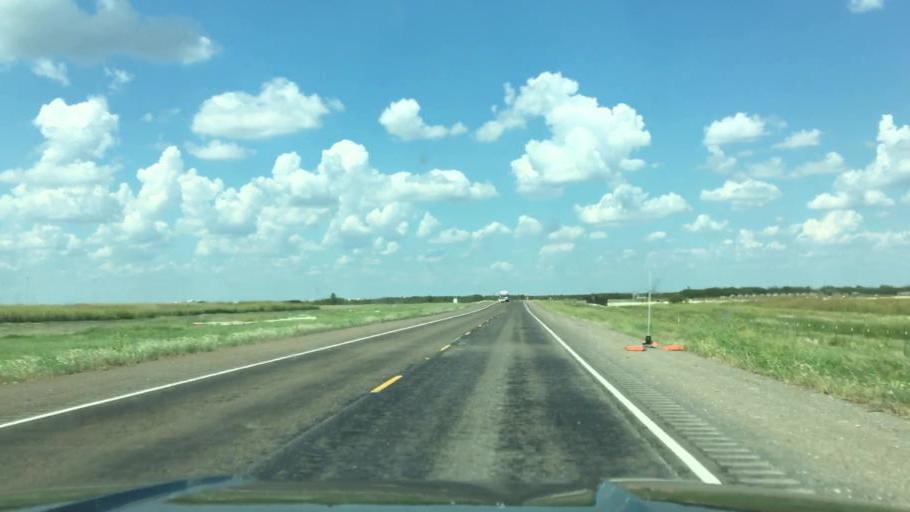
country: US
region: Texas
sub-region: Tarrant County
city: Haslet
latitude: 32.9968
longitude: -97.3424
